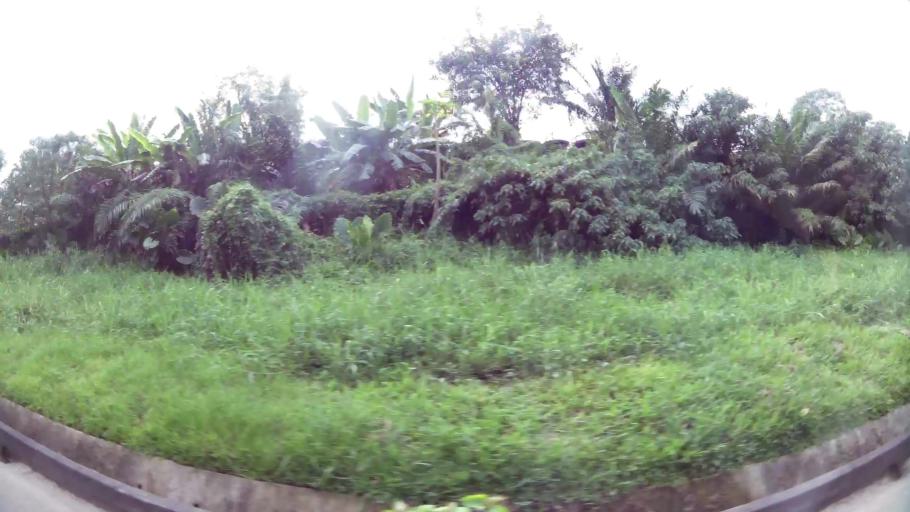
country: MY
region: Johor
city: Johor Bahru
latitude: 1.4405
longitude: 103.7079
